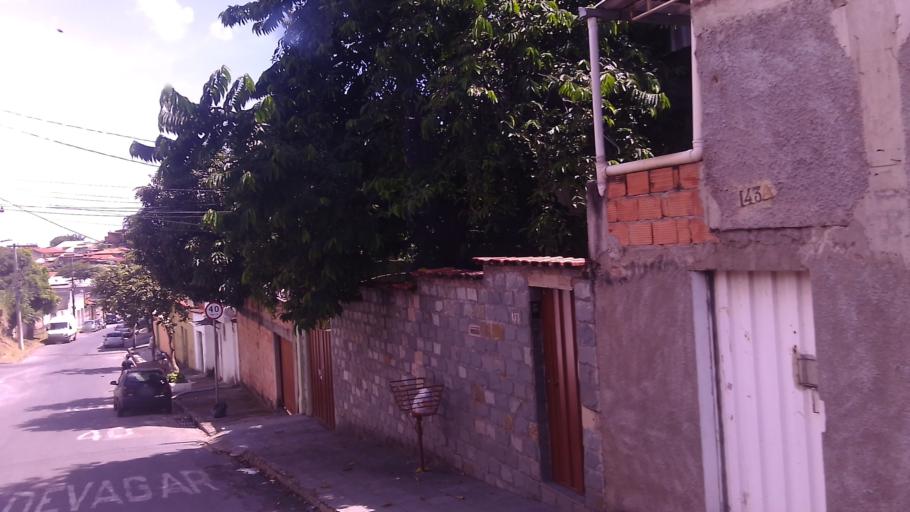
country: BR
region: Minas Gerais
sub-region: Contagem
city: Contagem
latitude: -19.9154
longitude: -43.9978
